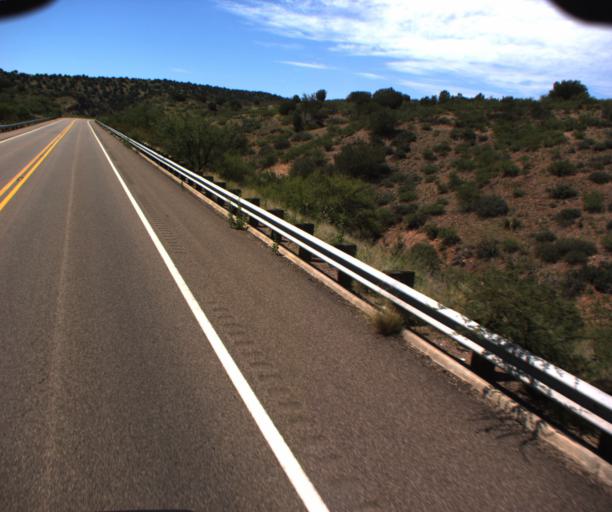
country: US
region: Arizona
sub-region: Gila County
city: Globe
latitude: 33.5811
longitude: -110.6521
